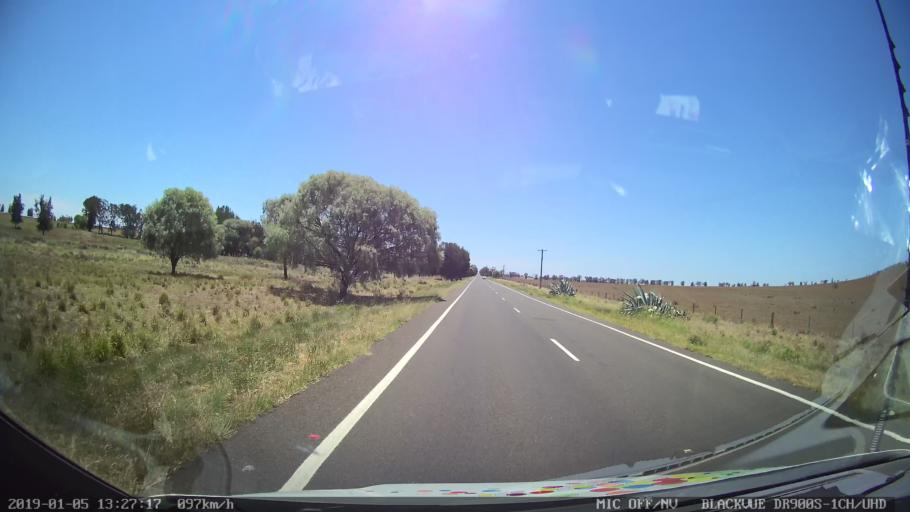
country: AU
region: New South Wales
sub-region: Gunnedah
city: Gunnedah
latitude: -31.0459
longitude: 150.0272
